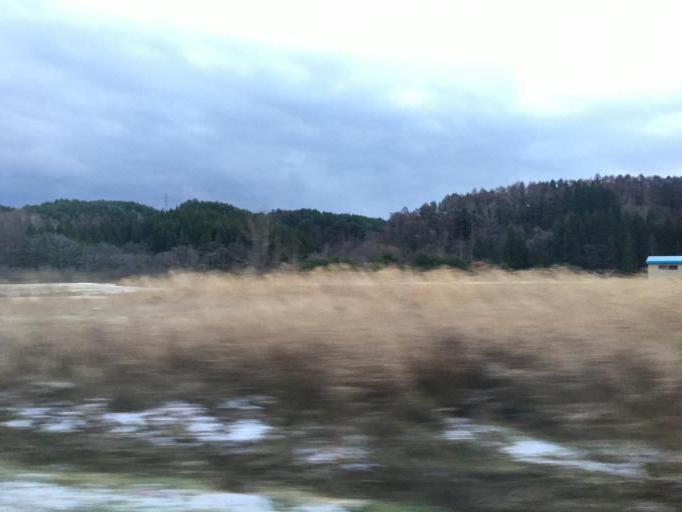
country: JP
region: Aomori
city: Aomori Shi
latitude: 40.8213
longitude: 140.6557
